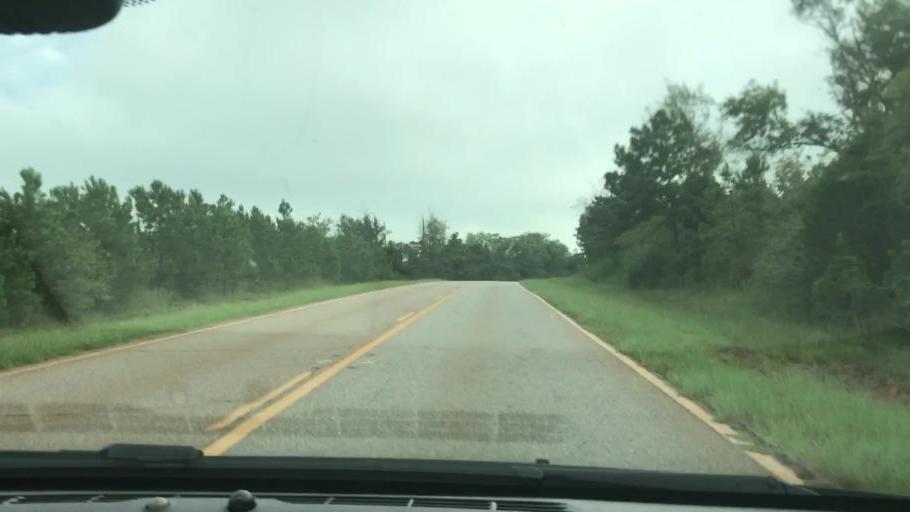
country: US
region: Georgia
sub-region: Quitman County
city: Georgetown
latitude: 31.9708
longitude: -84.9842
